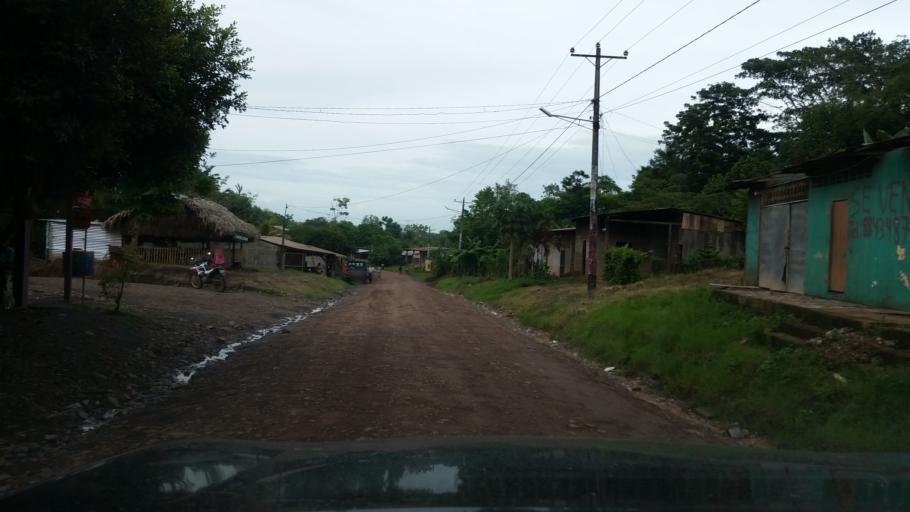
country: NI
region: Matagalpa
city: Rio Blanco
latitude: 13.1745
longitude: -84.9542
